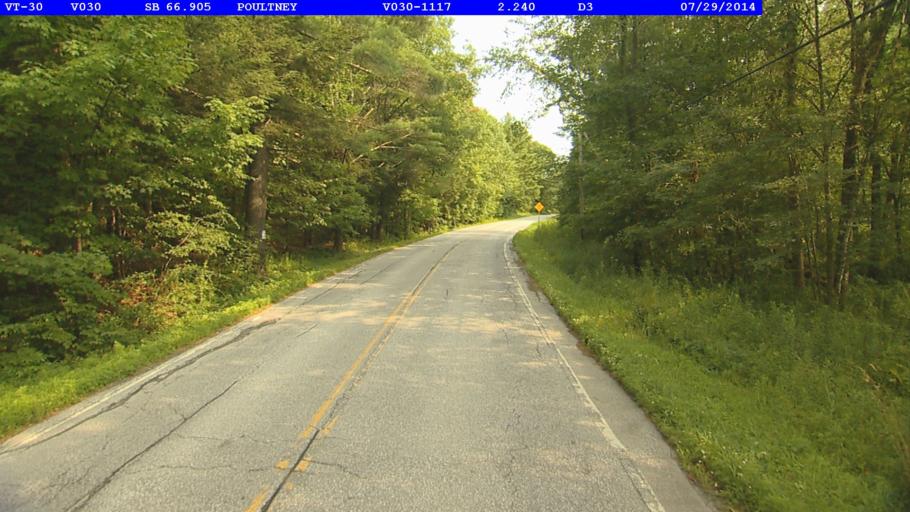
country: US
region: Vermont
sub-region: Rutland County
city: Poultney
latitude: 43.4945
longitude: -73.2053
